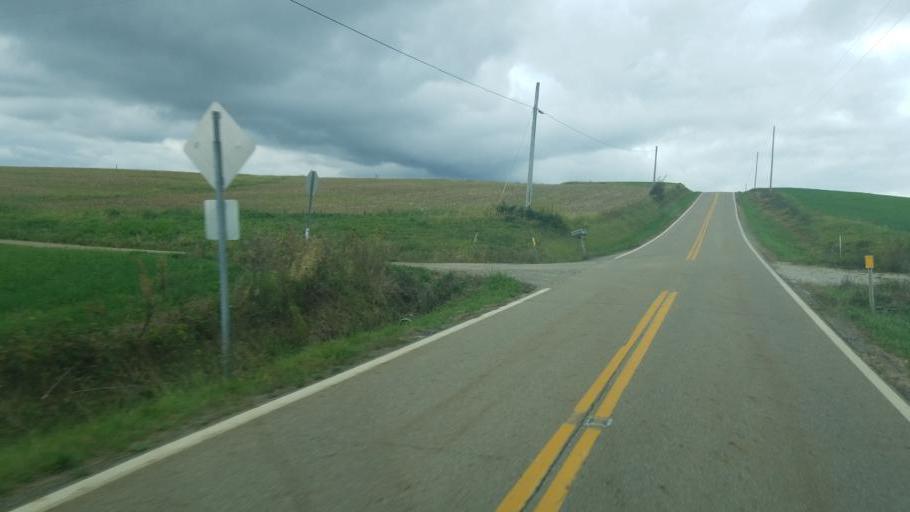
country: US
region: Ohio
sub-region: Ashland County
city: Loudonville
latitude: 40.5288
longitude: -82.1558
